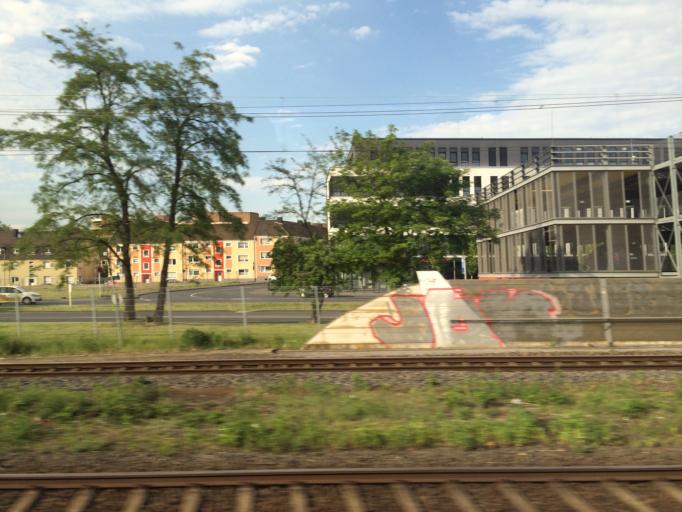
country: DE
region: North Rhine-Westphalia
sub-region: Regierungsbezirk Koln
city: Troisdorf
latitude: 50.8149
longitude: 7.1475
